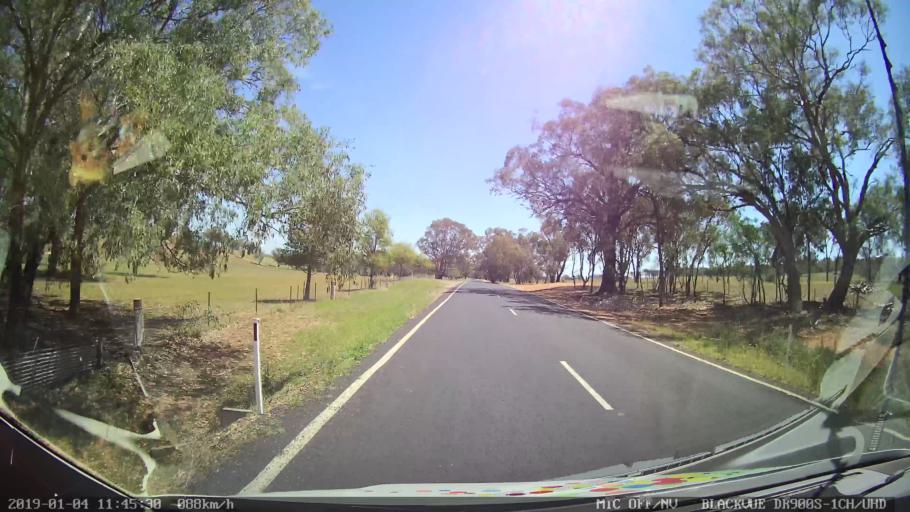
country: AU
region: New South Wales
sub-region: Cabonne
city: Molong
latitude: -32.9528
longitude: 148.7632
